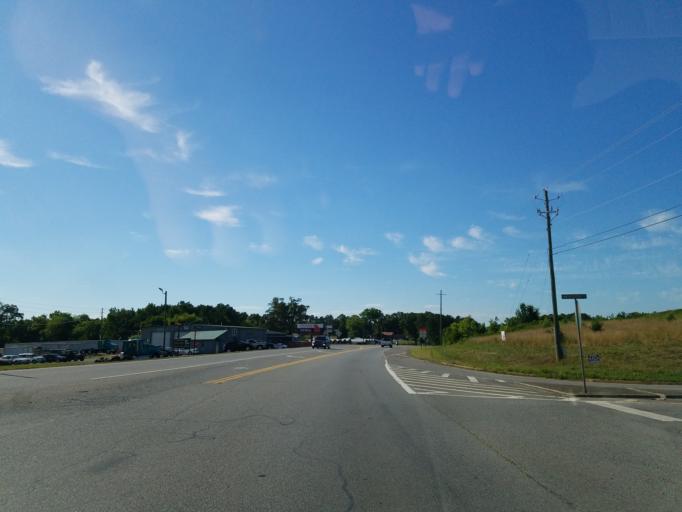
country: US
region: Georgia
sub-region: Bartow County
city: Adairsville
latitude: 34.3793
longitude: -84.9342
